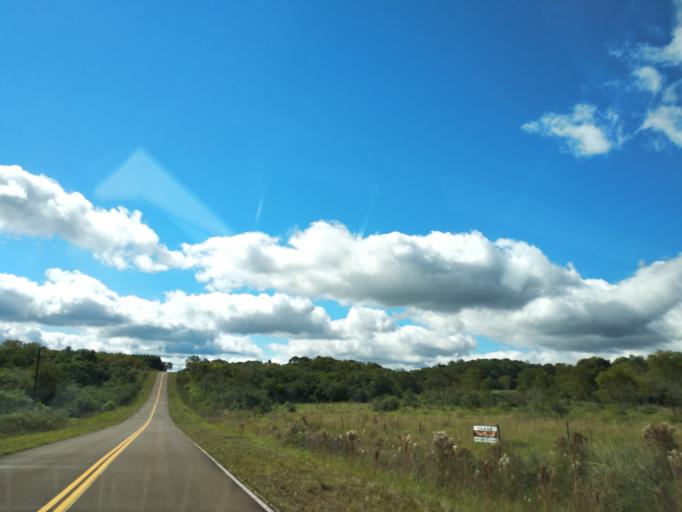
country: AR
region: Misiones
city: Santa Ana
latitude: -27.4111
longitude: -55.5577
